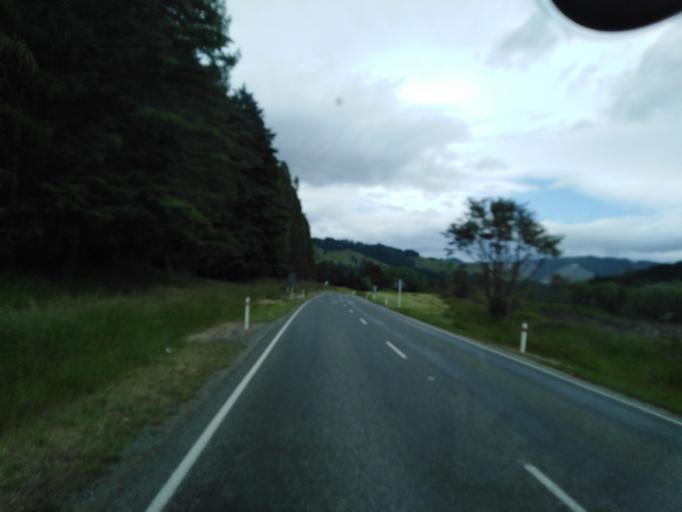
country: NZ
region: Tasman
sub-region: Tasman District
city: Wakefield
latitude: -41.4749
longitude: 172.8502
